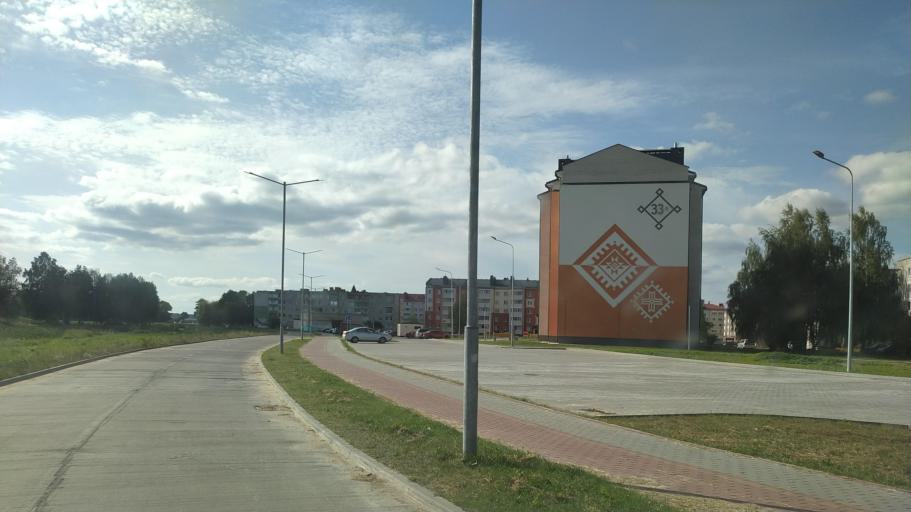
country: BY
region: Brest
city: Byaroza
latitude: 52.5352
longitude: 24.9955
